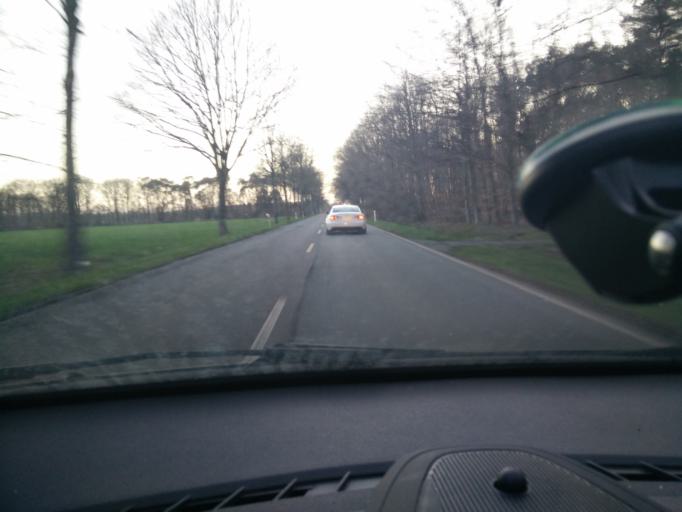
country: DE
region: North Rhine-Westphalia
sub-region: Regierungsbezirk Munster
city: Raesfeld
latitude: 51.7522
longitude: 6.7559
